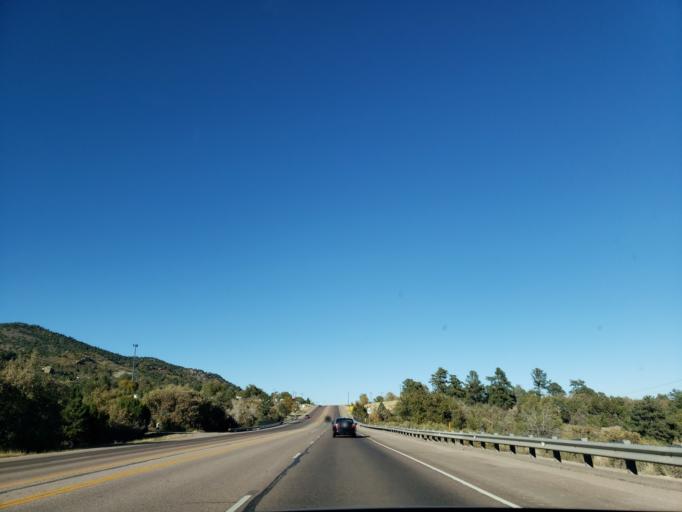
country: US
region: Colorado
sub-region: El Paso County
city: Fort Carson
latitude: 38.6758
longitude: -104.8499
